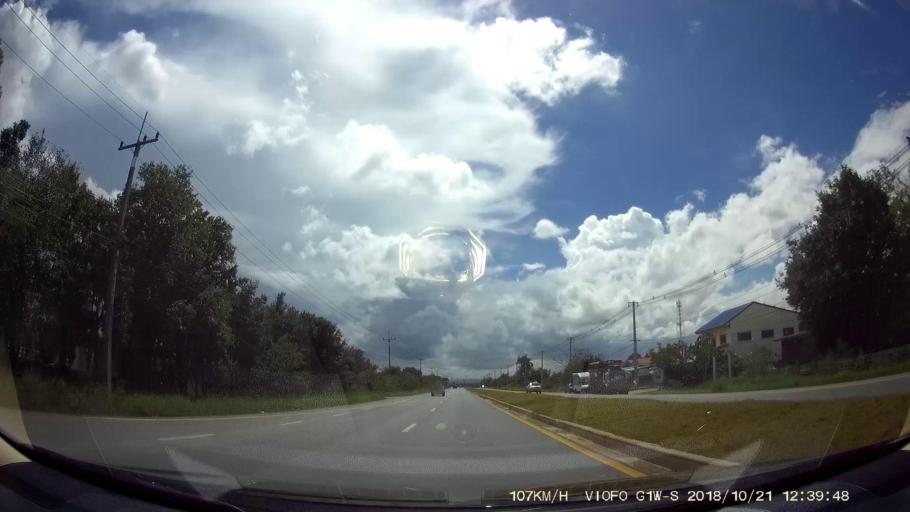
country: TH
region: Nakhon Ratchasima
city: Amphoe Sikhiu
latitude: 15.0339
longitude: 101.6989
